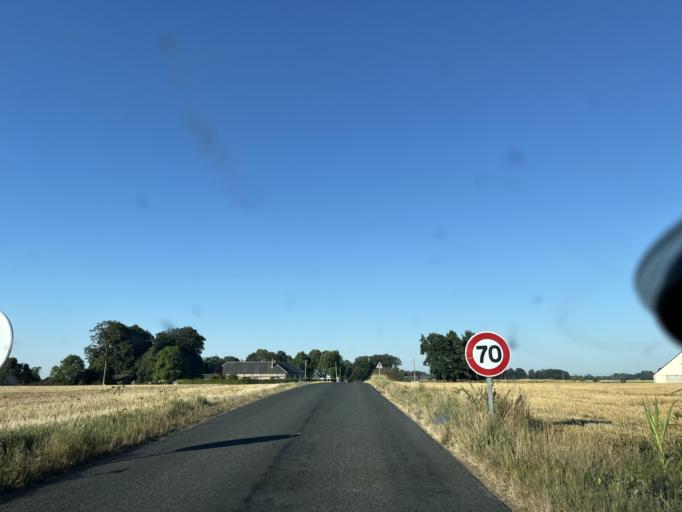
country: FR
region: Haute-Normandie
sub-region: Departement de la Seine-Maritime
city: Lanquetot
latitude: 49.5624
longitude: 0.5845
